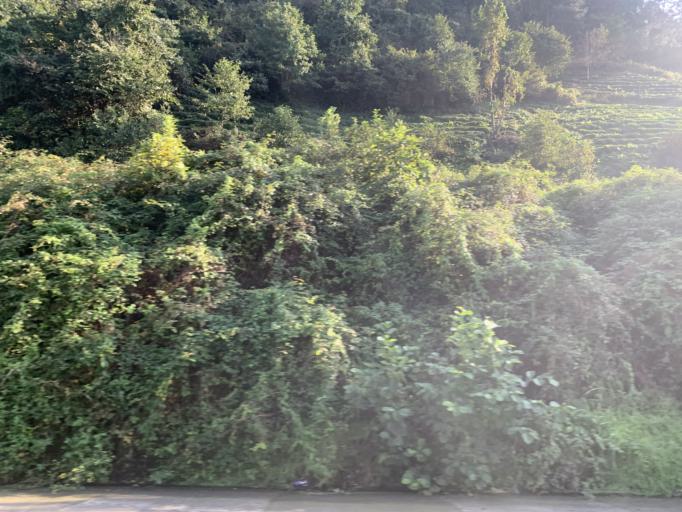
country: TR
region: Trabzon
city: Of
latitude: 40.9268
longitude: 40.2285
